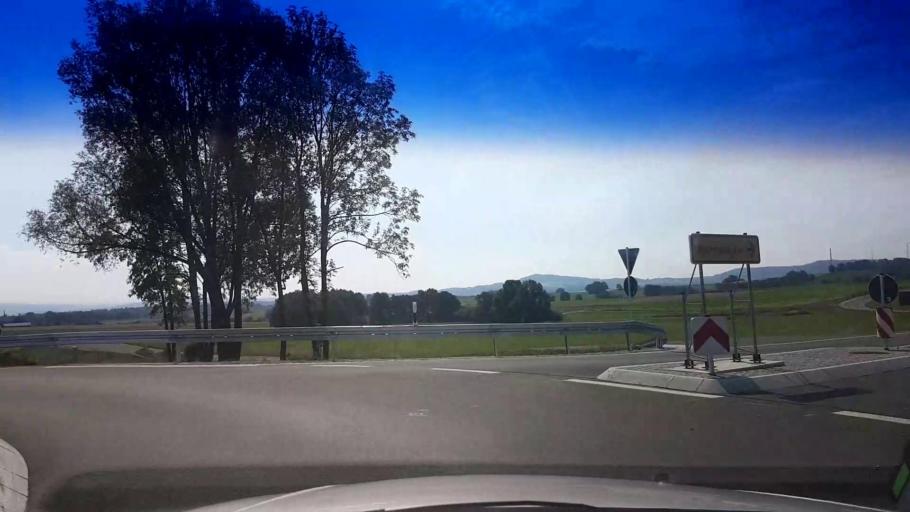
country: DE
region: Bavaria
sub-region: Upper Franconia
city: Mistelgau
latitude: 49.9298
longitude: 11.4755
